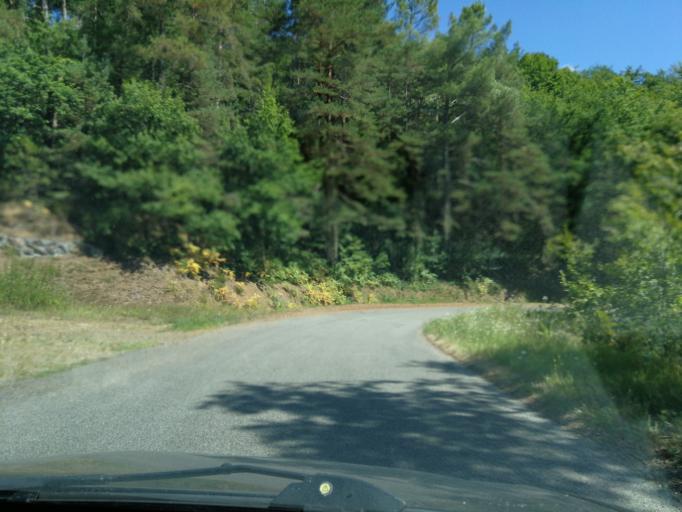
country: FR
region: Limousin
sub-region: Departement de la Correze
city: Argentat
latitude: 45.0922
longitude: 1.8990
